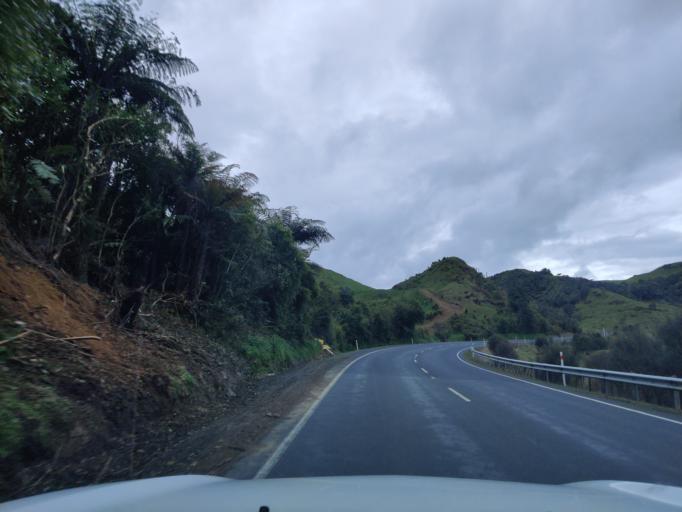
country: NZ
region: Waikato
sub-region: Otorohanga District
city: Otorohanga
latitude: -38.5166
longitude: 175.2074
